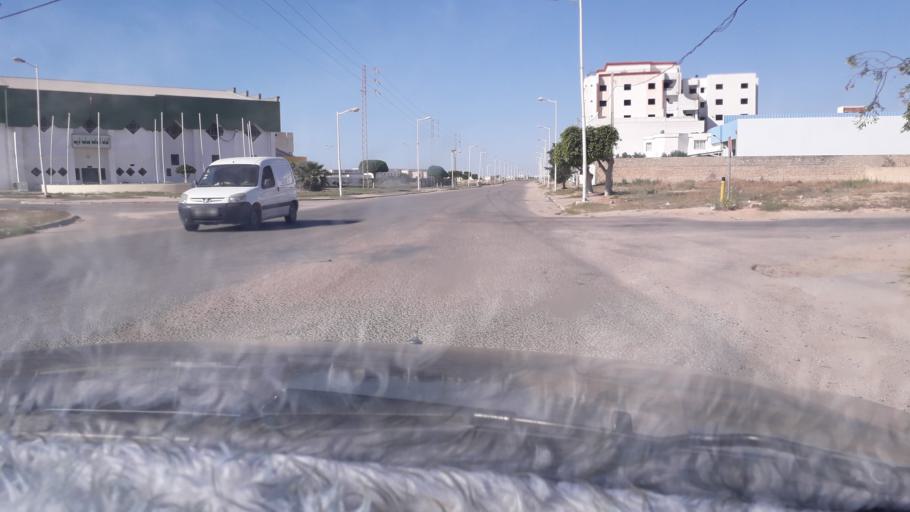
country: TN
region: Safaqis
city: Al Qarmadah
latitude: 34.8437
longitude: 10.7575
